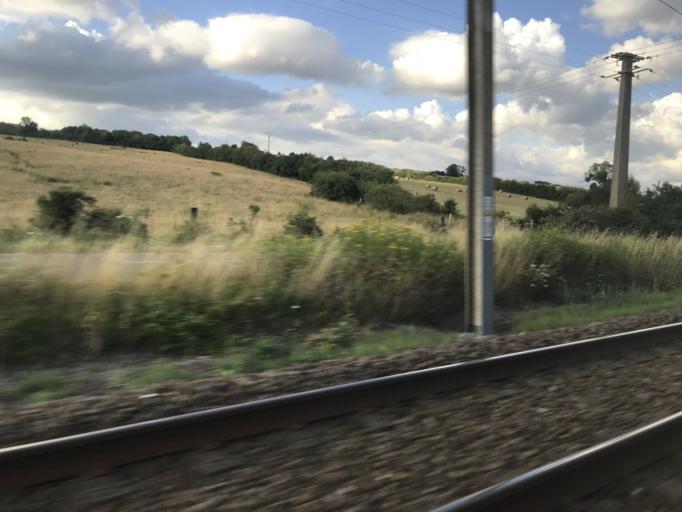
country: FR
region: Champagne-Ardenne
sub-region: Departement des Ardennes
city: Dom-le-Mesnil
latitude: 49.6985
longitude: 4.8245
